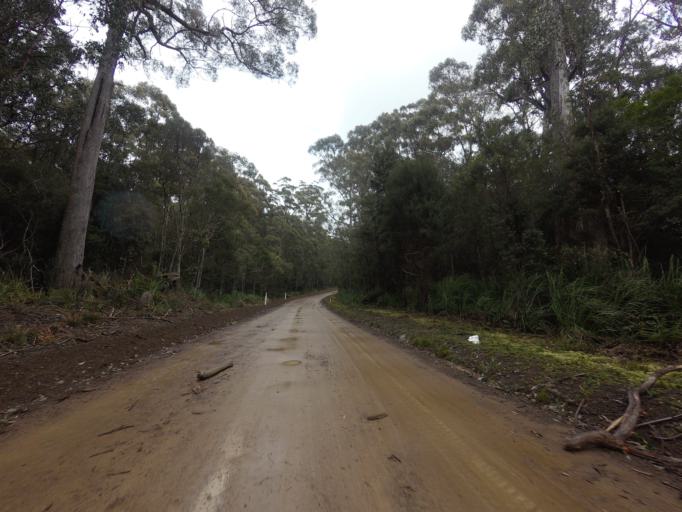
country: AU
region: Tasmania
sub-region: Huon Valley
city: Geeveston
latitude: -43.5280
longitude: 146.8907
